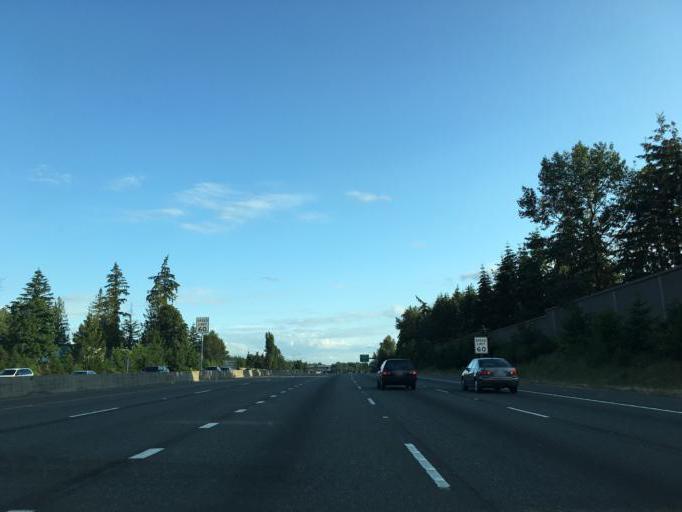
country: US
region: Washington
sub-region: King County
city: Kirkland
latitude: 47.6892
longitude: -122.1820
